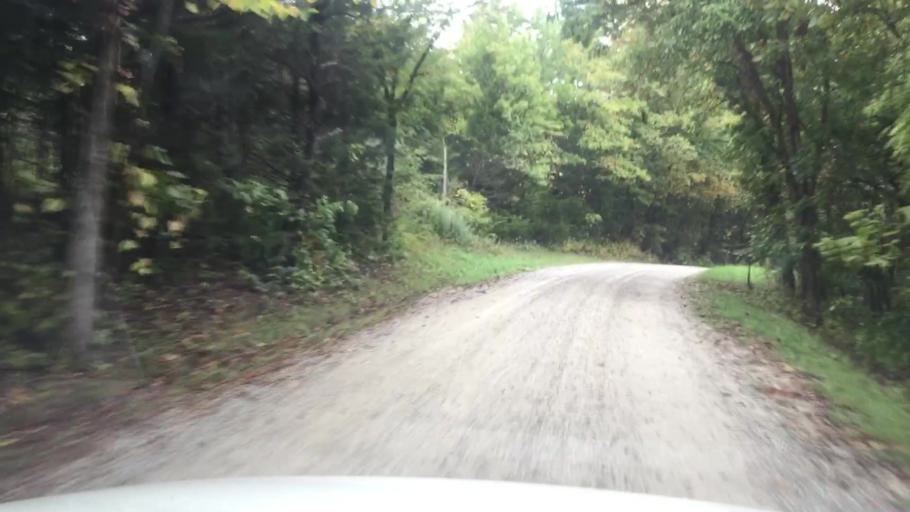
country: US
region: Missouri
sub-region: Boone County
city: Ashland
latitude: 38.8231
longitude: -92.3338
